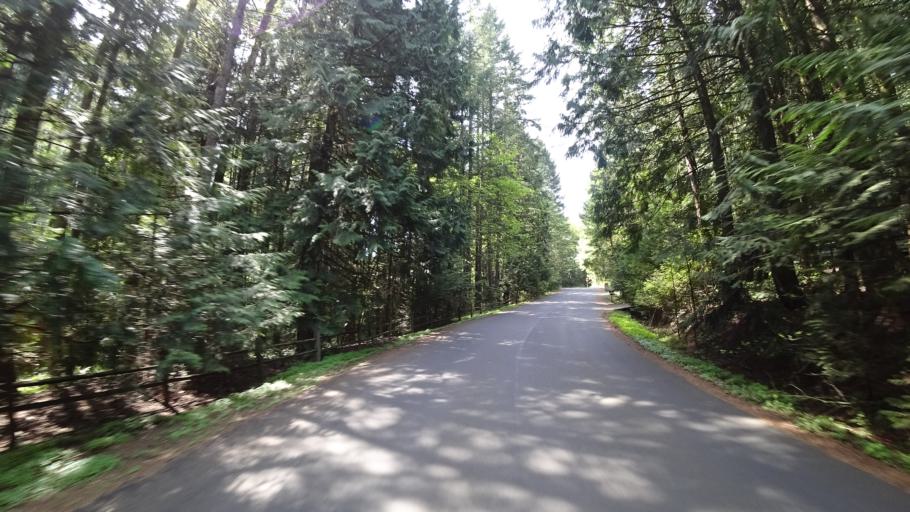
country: US
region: Oregon
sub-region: Washington County
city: Aloha
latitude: 45.4521
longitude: -122.8531
